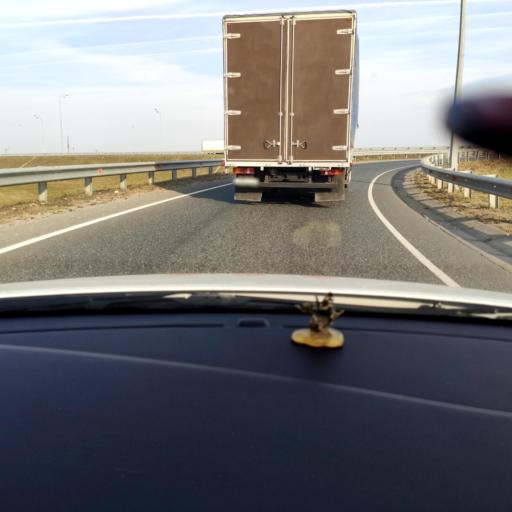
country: RU
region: Tatarstan
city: Osinovo
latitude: 55.8576
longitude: 48.8522
